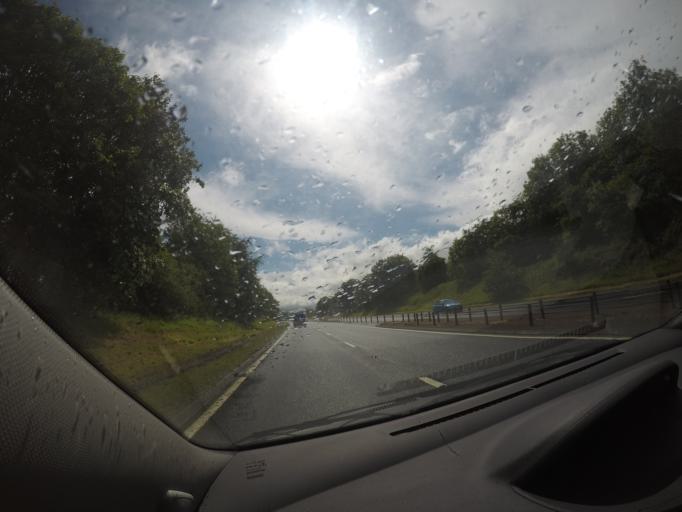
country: GB
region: Scotland
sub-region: Perth and Kinross
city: Auchterarder
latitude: 56.3179
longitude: -3.6528
